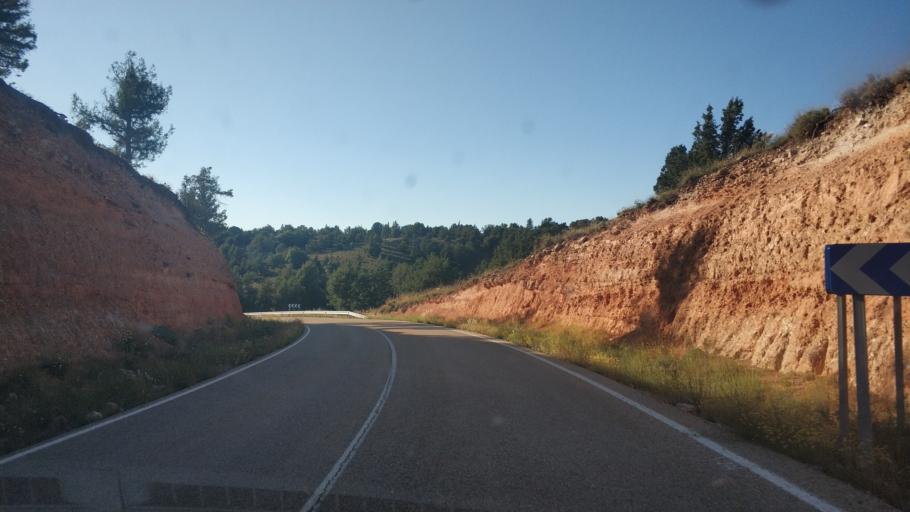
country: ES
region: Castille and Leon
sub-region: Provincia de Soria
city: Montejo de Tiermes
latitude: 41.4335
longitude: -3.2050
